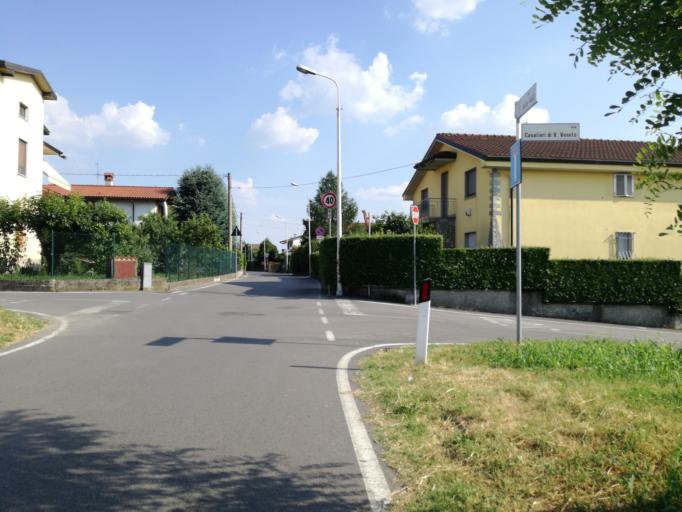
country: IT
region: Lombardy
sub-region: Provincia di Bergamo
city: Calusco d'Adda
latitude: 45.6867
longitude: 9.4581
